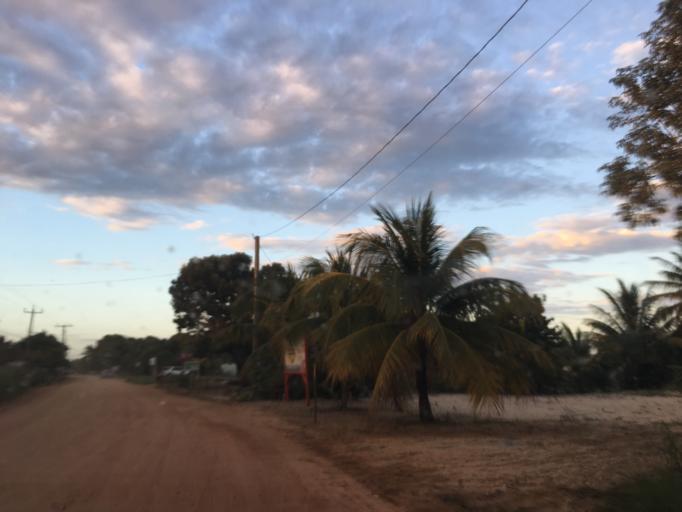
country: BZ
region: Stann Creek
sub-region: Dangriga
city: Dangriga
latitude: 16.8508
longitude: -88.2791
